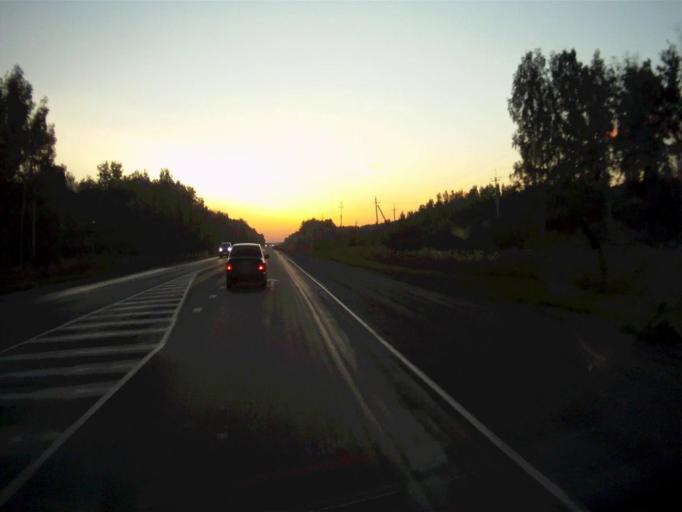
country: RU
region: Chelyabinsk
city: Poletayevo
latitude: 55.2084
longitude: 61.0942
